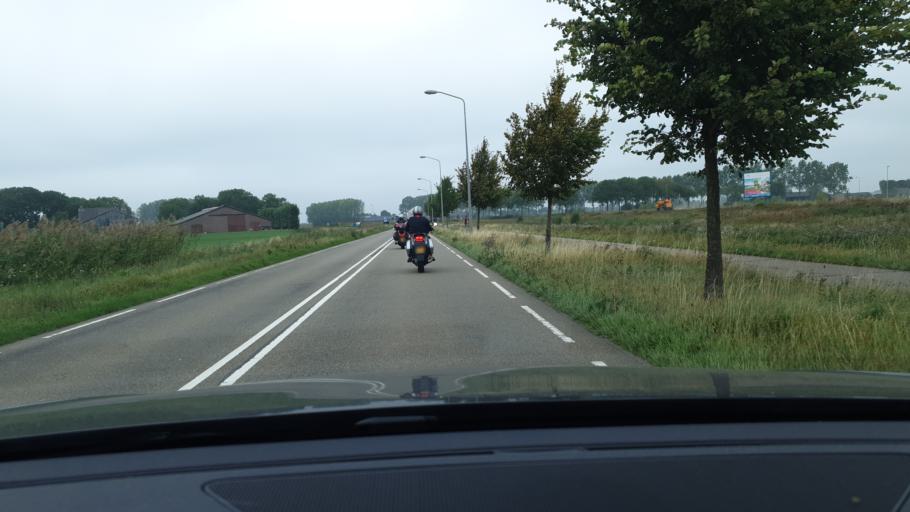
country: NL
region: North Brabant
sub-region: Gemeente 's-Hertogenbosch
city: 's-Hertogenbosch
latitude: 51.7371
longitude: 5.3452
